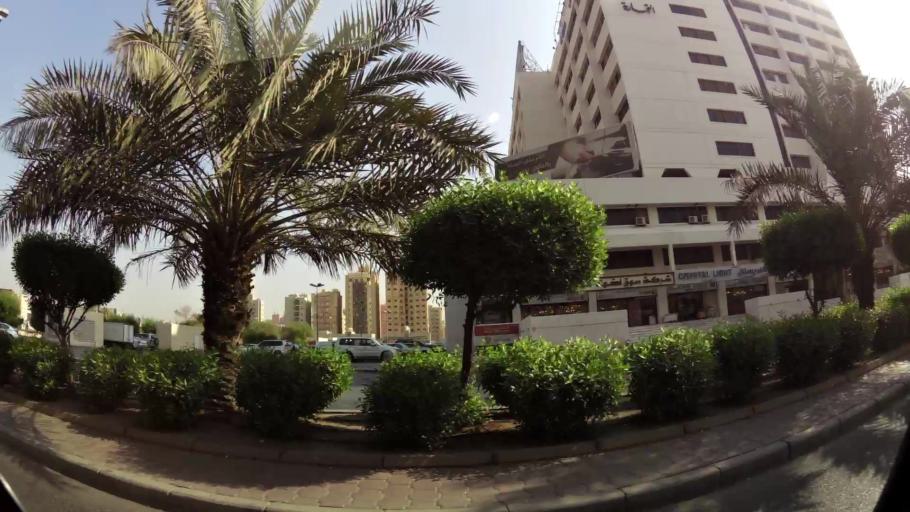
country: KW
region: Muhafazat Hawalli
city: Hawalli
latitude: 29.3359
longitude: 48.0249
